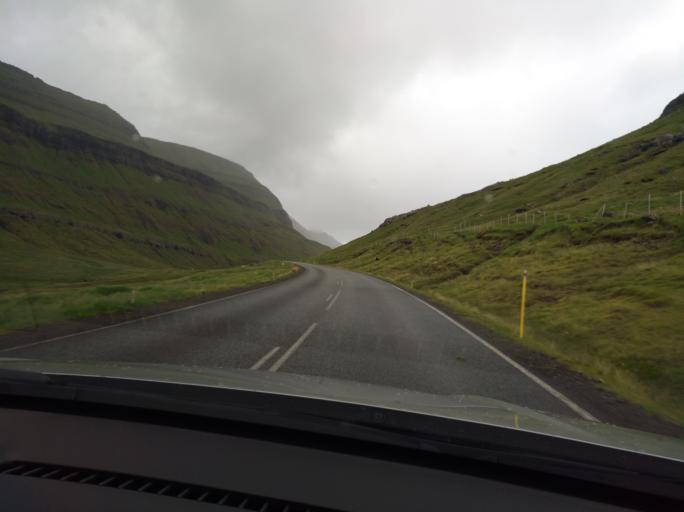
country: FO
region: Eysturoy
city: Fuglafjordur
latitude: 62.2293
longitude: -6.8790
